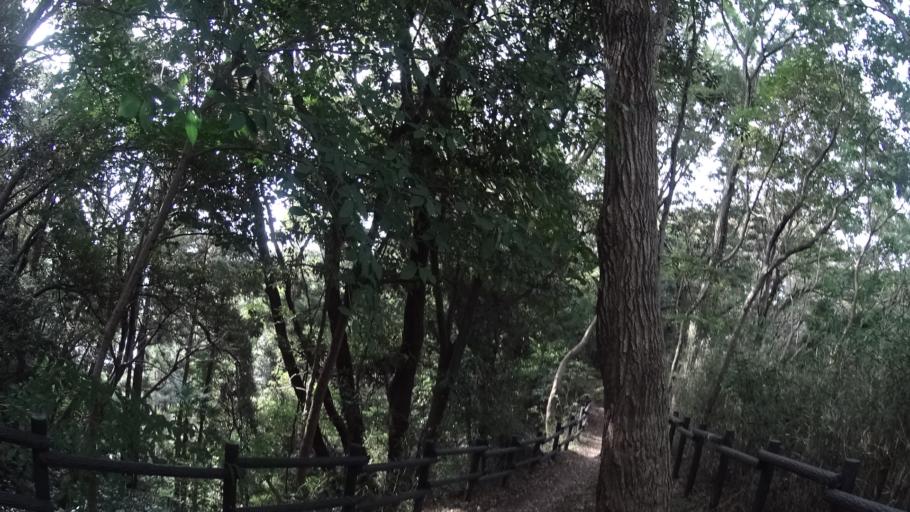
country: JP
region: Kanagawa
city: Zushi
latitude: 35.3533
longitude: 139.6012
